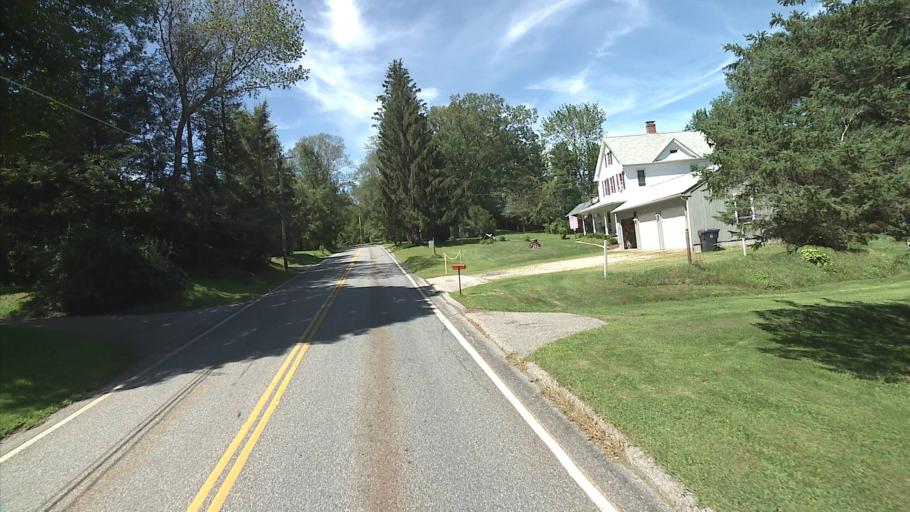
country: US
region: Connecticut
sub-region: Windham County
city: South Woodstock
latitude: 41.8715
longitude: -71.9642
